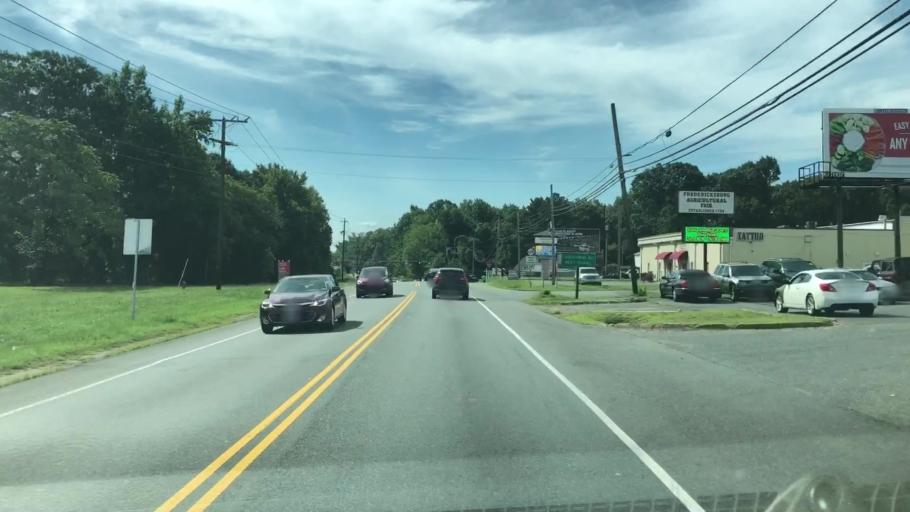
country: US
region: Virginia
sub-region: City of Fredericksburg
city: Fredericksburg
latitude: 38.2779
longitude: -77.4526
